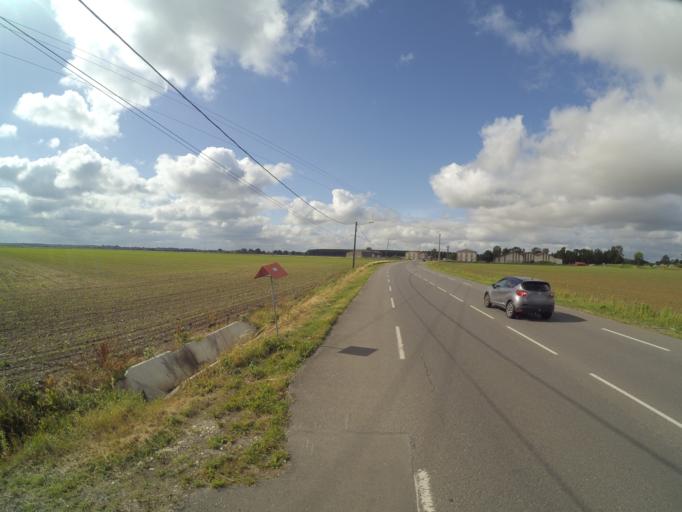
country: FR
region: Aquitaine
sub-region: Departement de la Gironde
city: Saint-Louis-de-Montferrand
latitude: 44.9279
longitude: -0.5624
